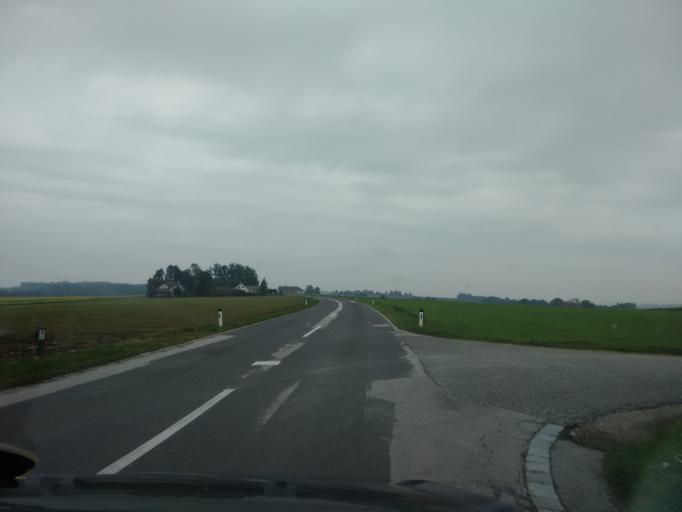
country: AT
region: Upper Austria
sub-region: Politischer Bezirk Kirchdorf an der Krems
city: Kremsmunster
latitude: 48.0361
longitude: 14.0929
